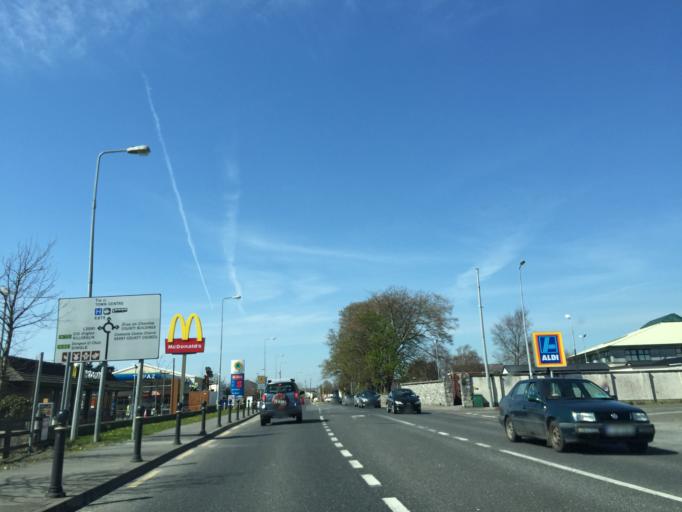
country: IE
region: Munster
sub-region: Ciarrai
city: Tralee
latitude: 52.2648
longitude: -9.6772
